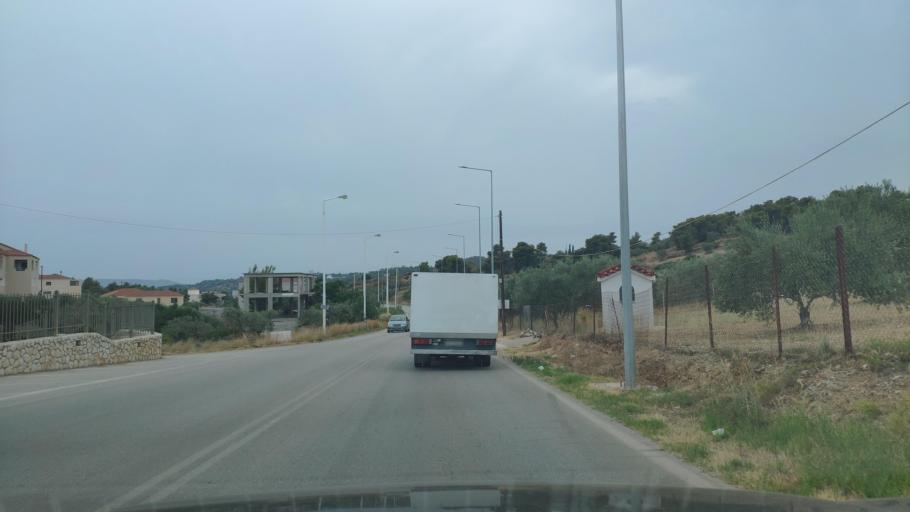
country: GR
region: Peloponnese
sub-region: Nomos Argolidos
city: Kranidi
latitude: 37.3603
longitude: 23.1623
